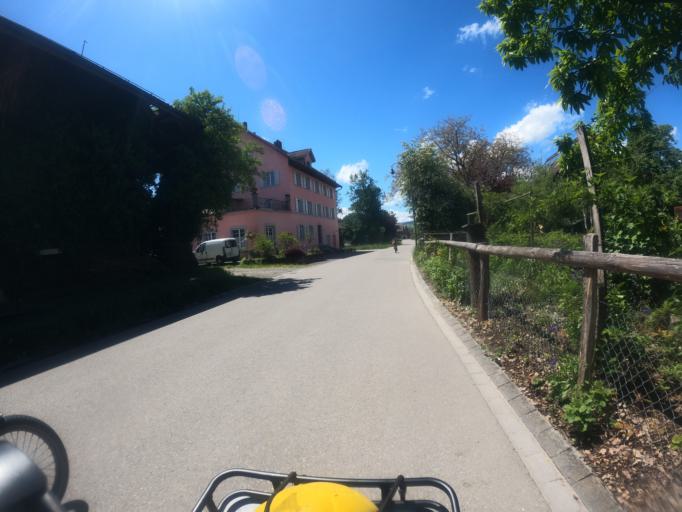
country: CH
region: Zurich
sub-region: Bezirk Affoltern
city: Obfelden / Oberlunnern
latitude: 47.2335
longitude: 8.4282
